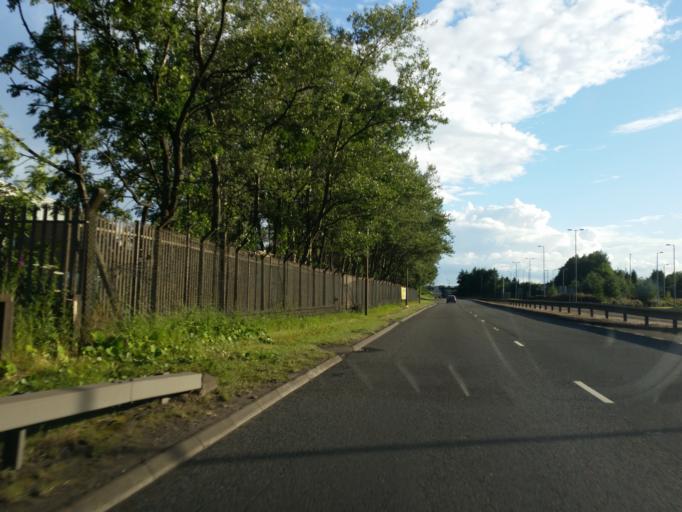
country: GB
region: Scotland
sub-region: North Lanarkshire
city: Bellshill
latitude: 55.8311
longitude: -4.0311
